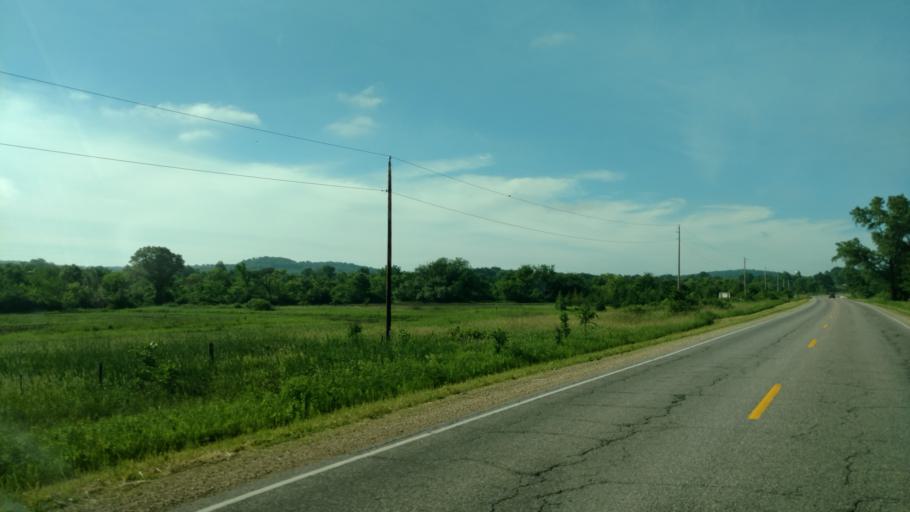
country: US
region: Wisconsin
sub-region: Sauk County
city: Reedsburg
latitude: 43.5667
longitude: -90.1331
